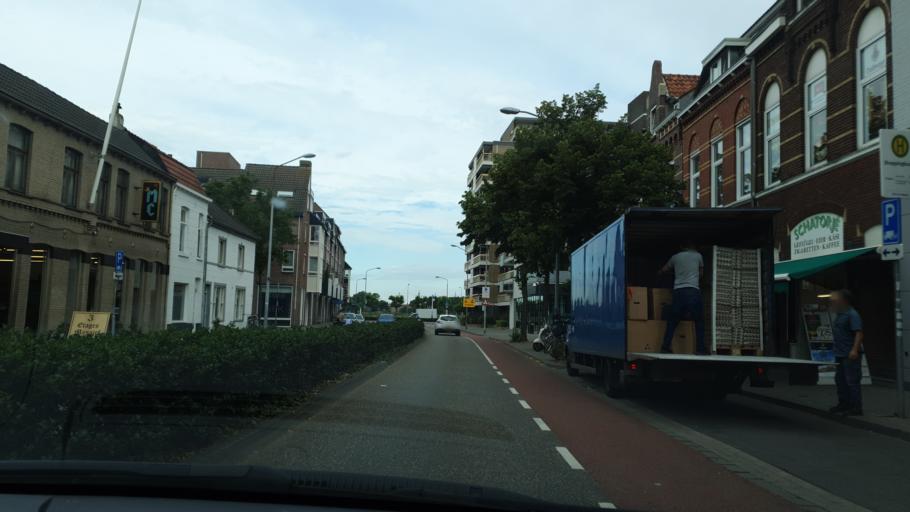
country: NL
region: Limburg
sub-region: Gemeente Venlo
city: Venlo
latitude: 51.3733
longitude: 6.1707
